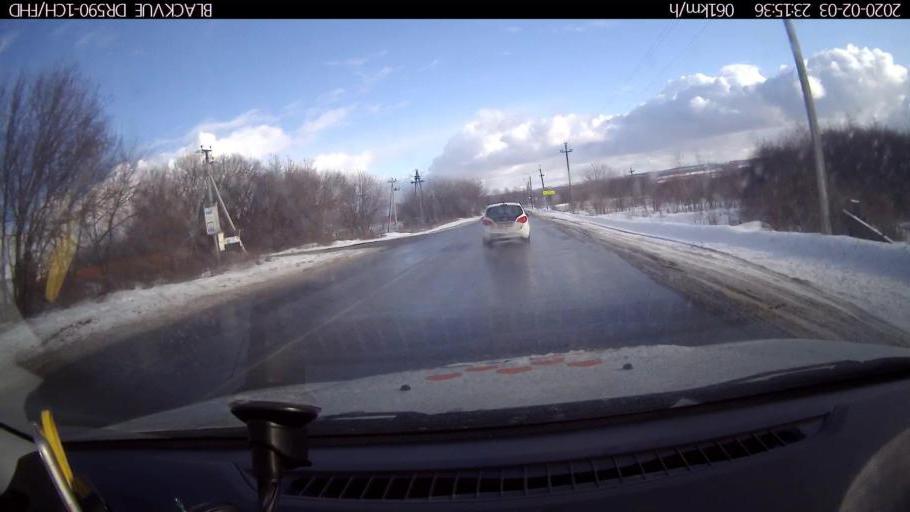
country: RU
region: Nizjnij Novgorod
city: Kstovo
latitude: 56.0844
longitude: 44.1392
